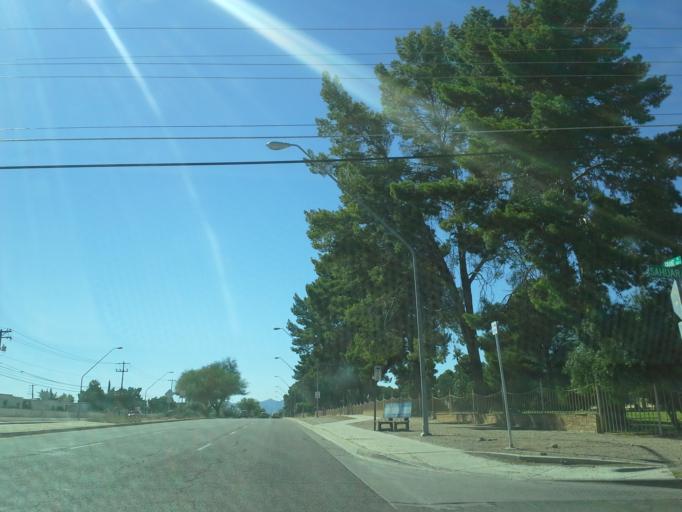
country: US
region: Arizona
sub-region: Pima County
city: Tucson
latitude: 32.2508
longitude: -110.8665
